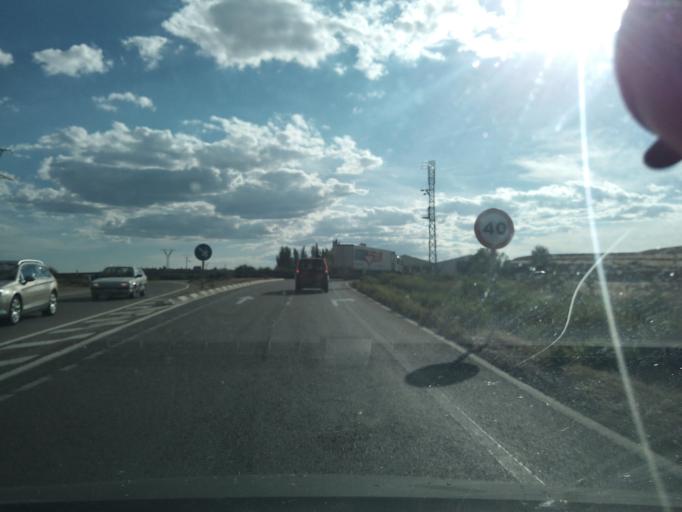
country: ES
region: Madrid
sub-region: Provincia de Madrid
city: Ajalvir
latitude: 40.5394
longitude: -3.4702
